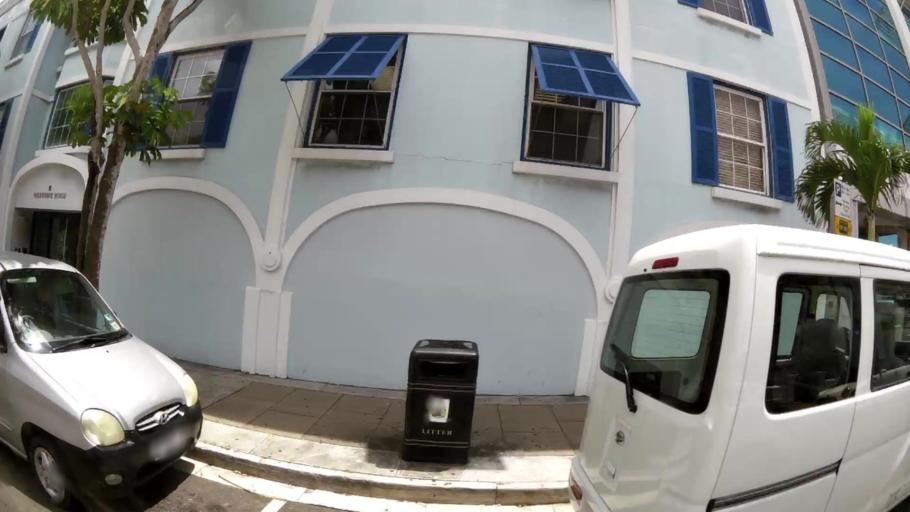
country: BM
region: Hamilton city
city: Hamilton
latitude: 32.2949
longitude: -64.7821
